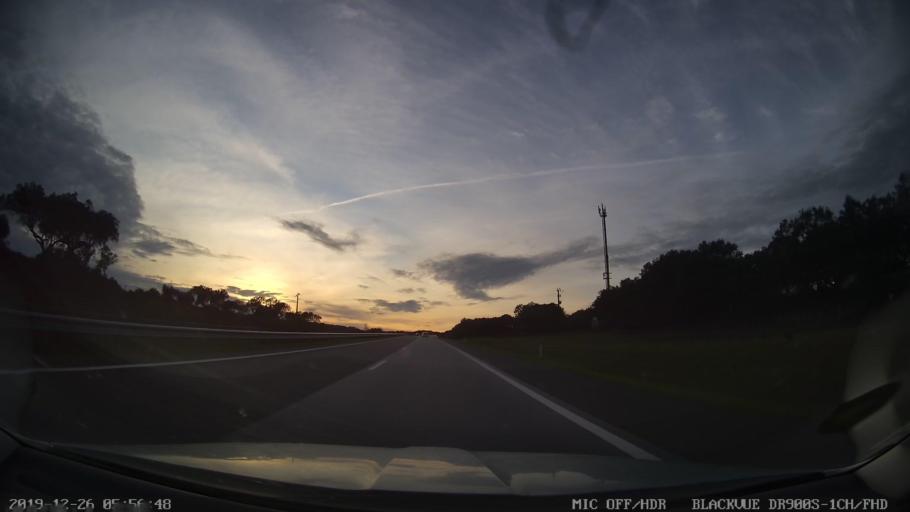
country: PT
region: Evora
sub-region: Evora
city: Evora
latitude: 38.6299
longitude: -7.9644
